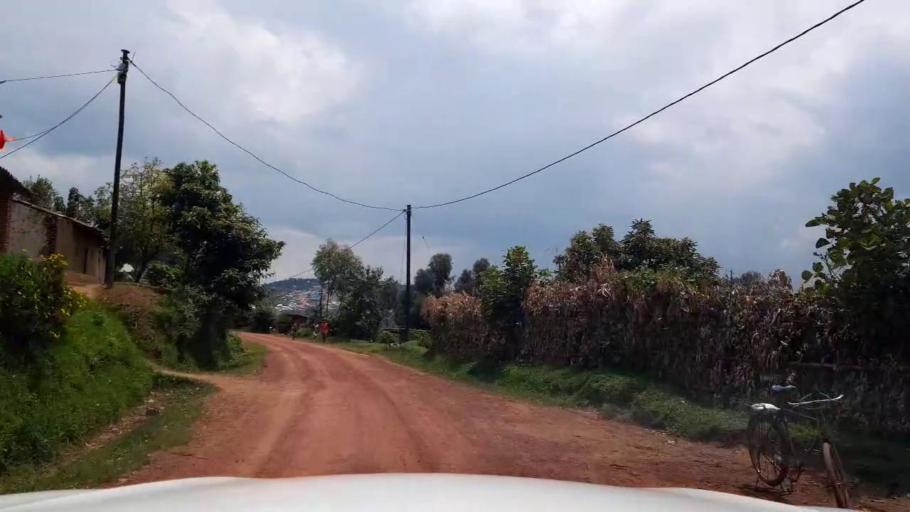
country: RW
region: Northern Province
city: Byumba
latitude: -1.4935
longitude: 29.9292
